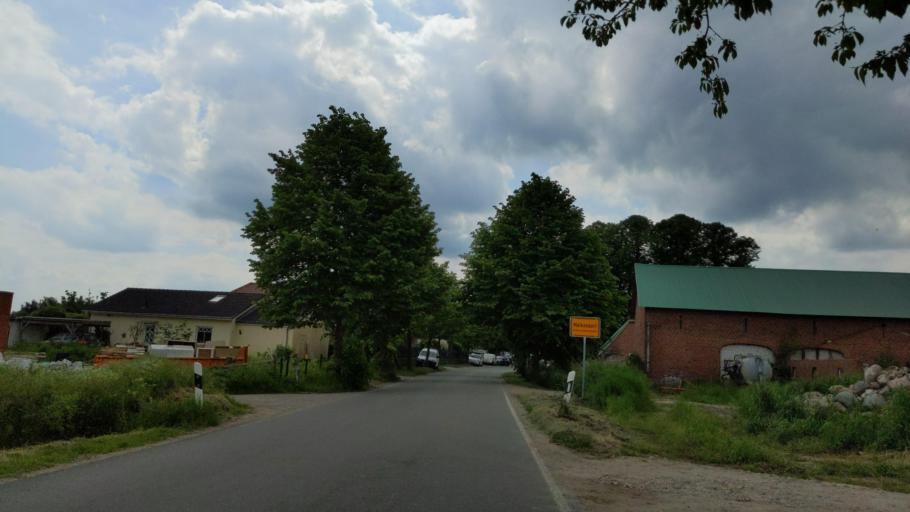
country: DE
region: Schleswig-Holstein
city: Bad Schwartau
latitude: 53.9677
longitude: 10.6609
